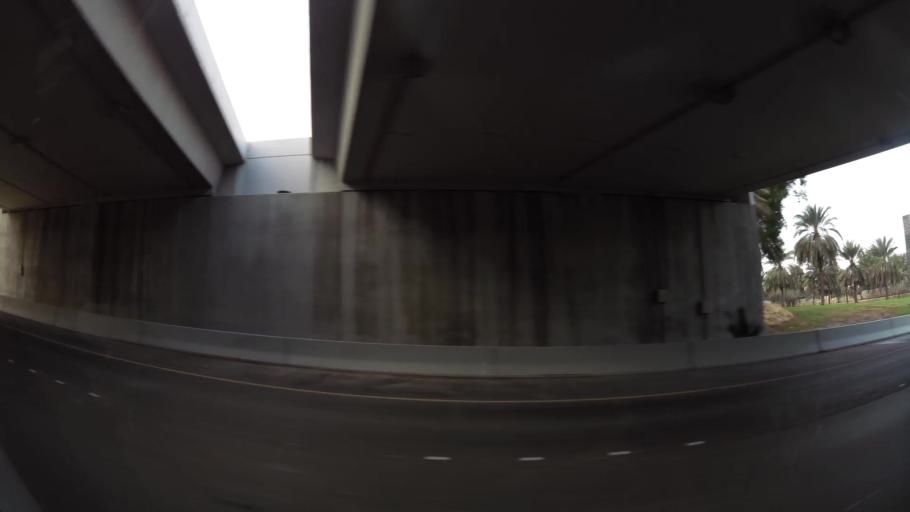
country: AE
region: Abu Dhabi
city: Abu Dhabi
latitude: 24.3928
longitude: 54.5240
